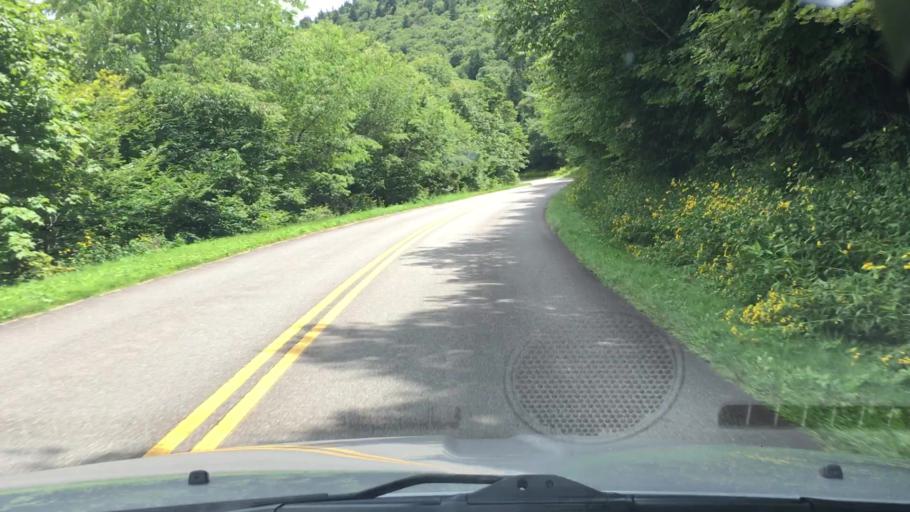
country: US
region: North Carolina
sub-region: Buncombe County
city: Black Mountain
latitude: 35.7103
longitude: -82.2739
